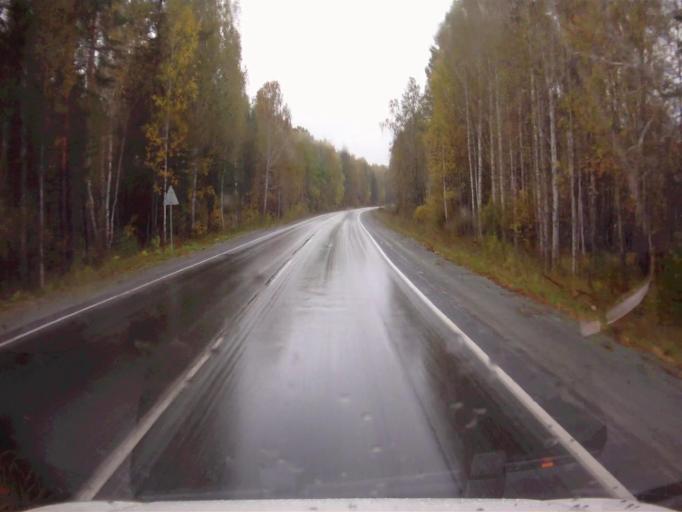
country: RU
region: Chelyabinsk
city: Tayginka
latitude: 55.5967
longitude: 60.6183
